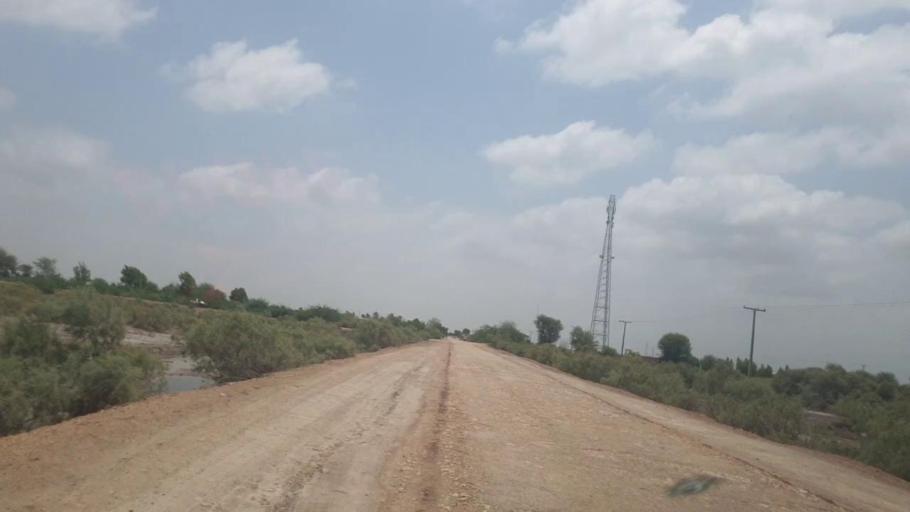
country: PK
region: Sindh
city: Tando Mittha Khan
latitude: 25.9173
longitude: 69.2234
